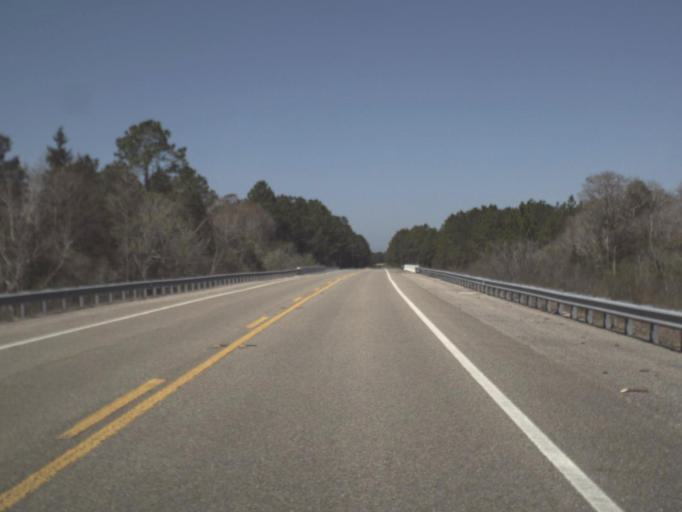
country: US
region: Florida
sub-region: Gulf County
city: Port Saint Joe
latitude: 29.7490
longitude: -85.2424
